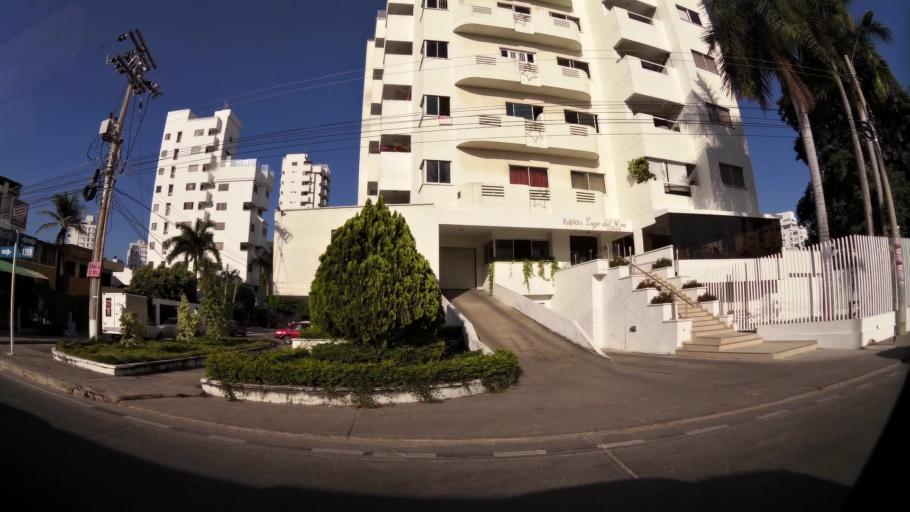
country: CO
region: Bolivar
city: Cartagena
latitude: 10.4171
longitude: -75.5341
